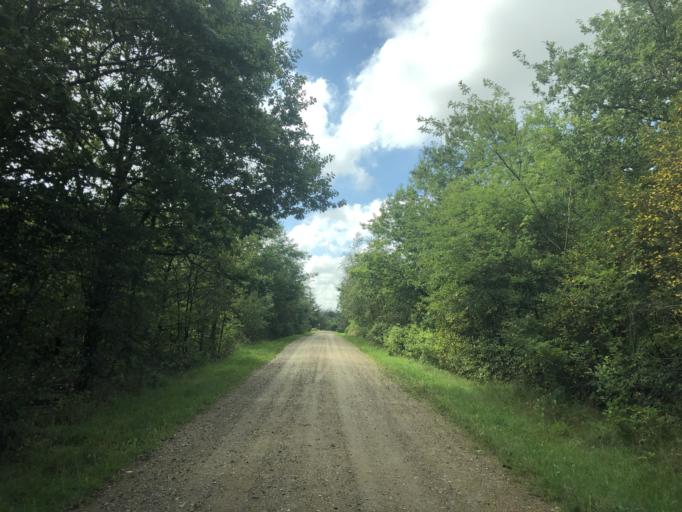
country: DK
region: Central Jutland
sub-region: Holstebro Kommune
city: Ulfborg
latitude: 56.2331
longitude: 8.4383
